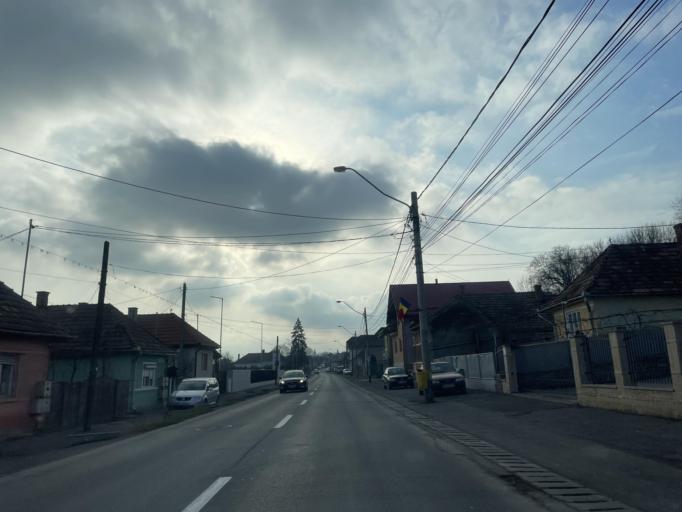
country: RO
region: Mures
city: Reghin-Sat
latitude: 46.7899
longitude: 24.7122
